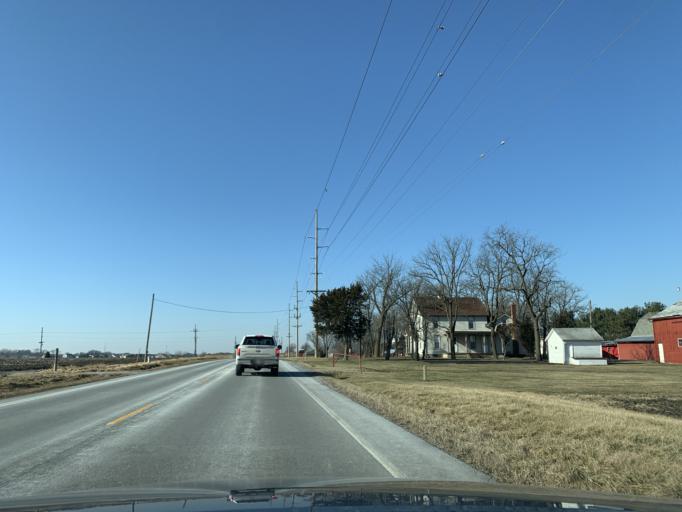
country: US
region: Indiana
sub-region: Lake County
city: Saint John
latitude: 41.4209
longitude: -87.4281
